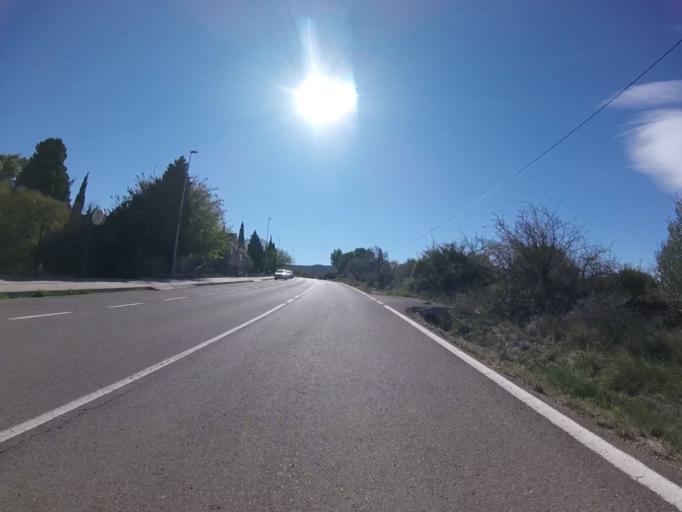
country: ES
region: Valencia
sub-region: Provincia de Castello
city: Albocasser
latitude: 40.3648
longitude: 0.0208
